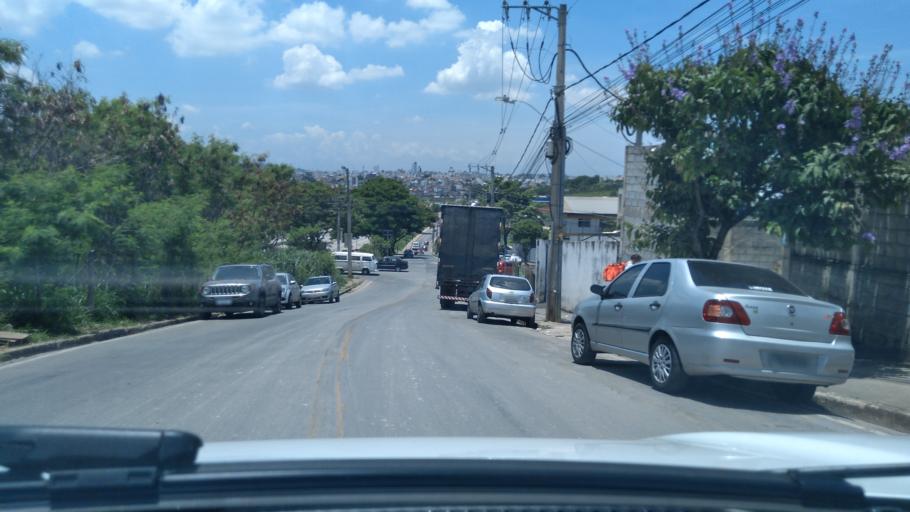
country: BR
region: Minas Gerais
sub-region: Contagem
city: Contagem
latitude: -19.9312
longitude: -44.0182
